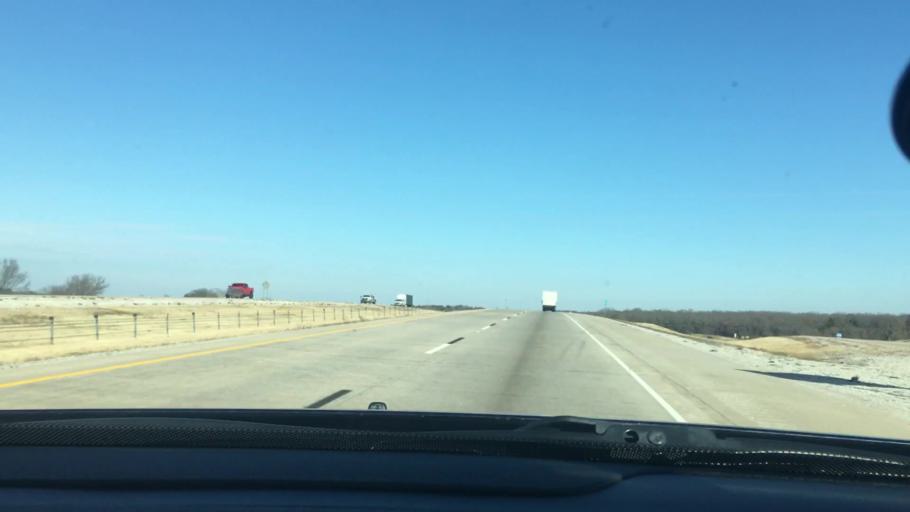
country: US
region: Oklahoma
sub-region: Carter County
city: Ardmore
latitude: 34.1359
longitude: -97.1557
